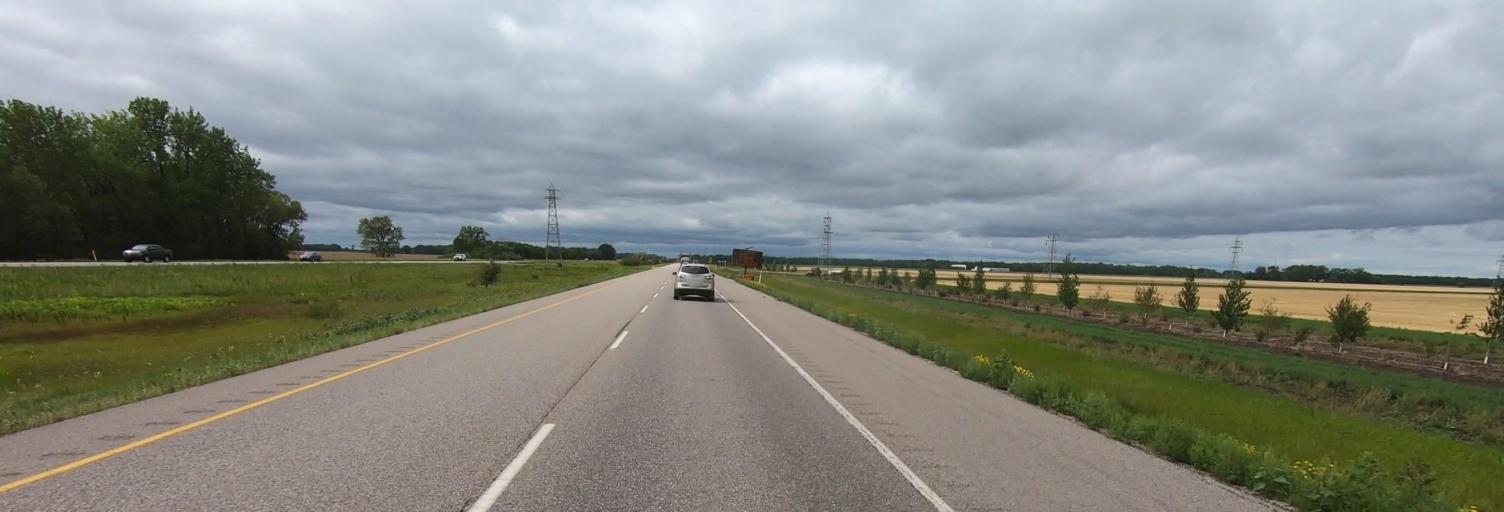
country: CA
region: Manitoba
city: Portage la Prairie
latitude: 49.9617
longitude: -98.0531
